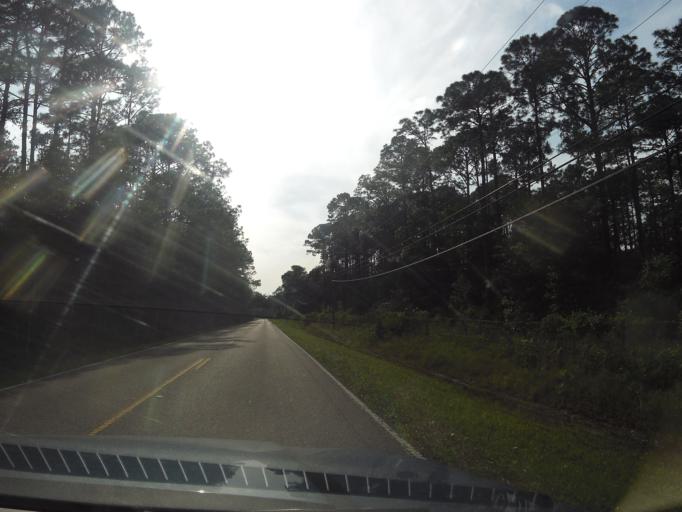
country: US
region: Florida
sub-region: Duval County
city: Atlantic Beach
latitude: 30.4585
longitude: -81.5221
